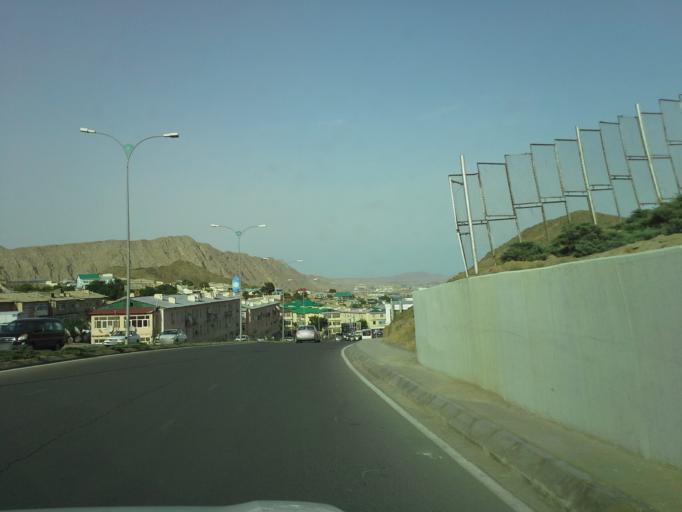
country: TM
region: Balkan
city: Turkmenbasy
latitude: 40.0021
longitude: 52.9797
